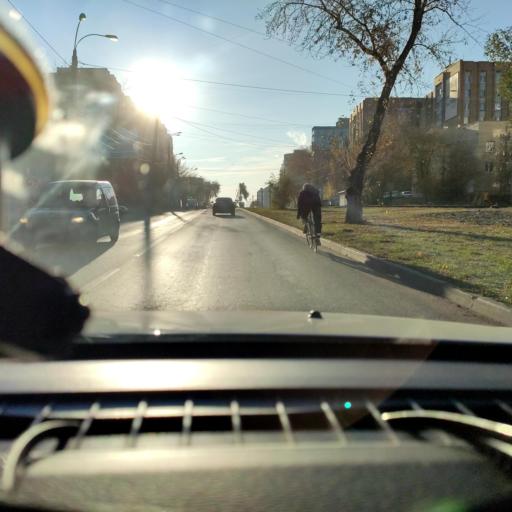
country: RU
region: Samara
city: Samara
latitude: 53.2017
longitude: 50.1509
